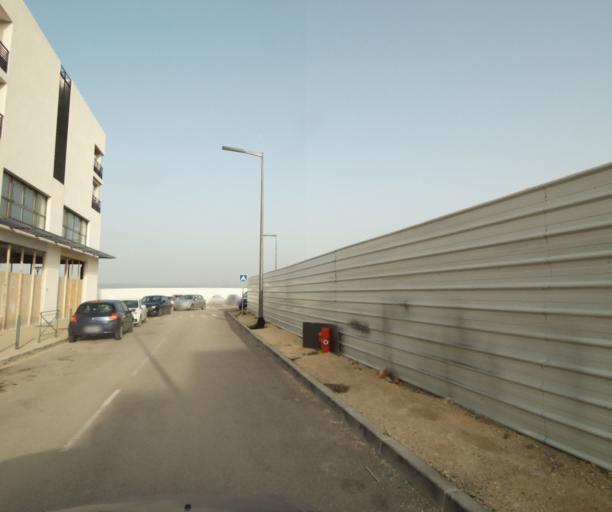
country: FR
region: Provence-Alpes-Cote d'Azur
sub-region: Departement des Bouches-du-Rhone
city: Cabries
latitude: 43.4857
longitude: 5.3486
